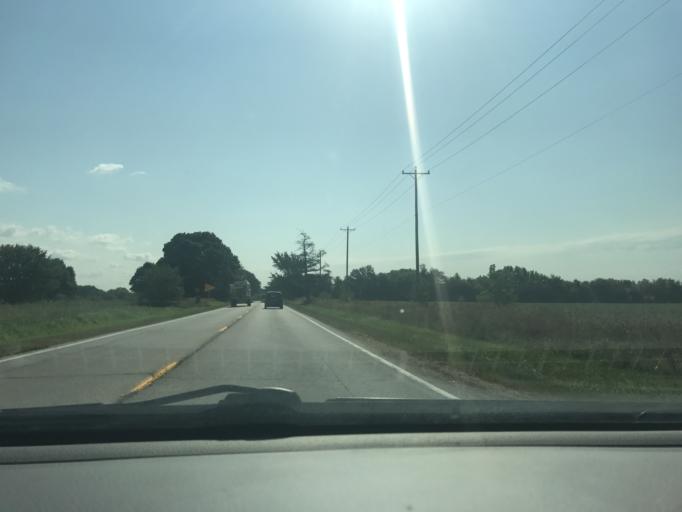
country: US
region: Illinois
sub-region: Kane County
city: Pingree Grove
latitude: 42.0462
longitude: -88.3861
